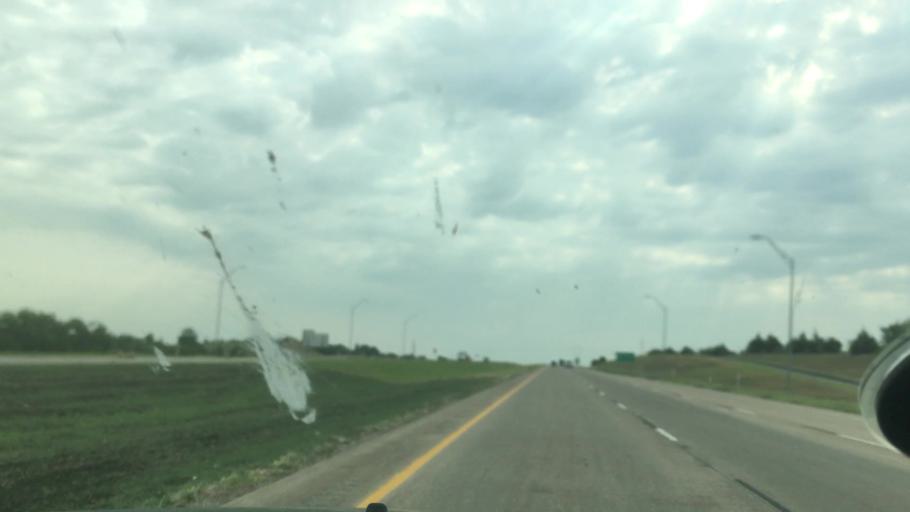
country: US
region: Texas
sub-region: Grayson County
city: Denison
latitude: 33.7909
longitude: -96.5672
